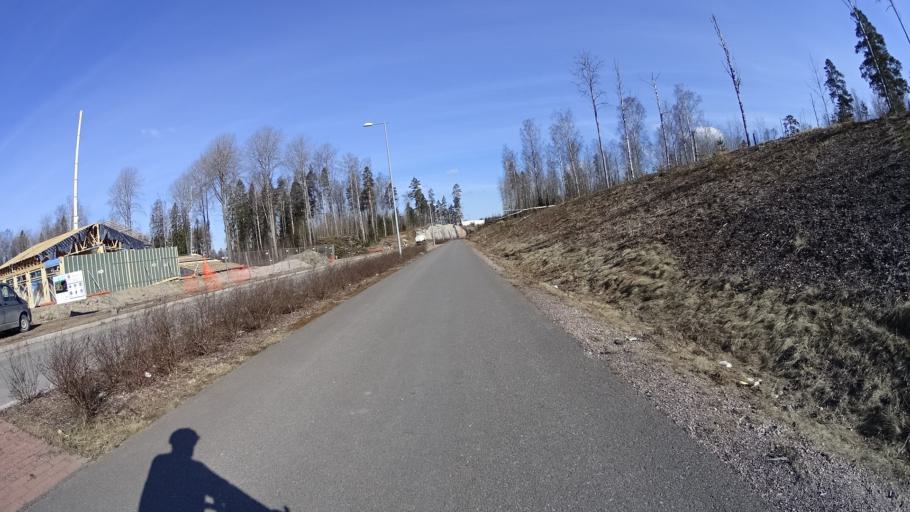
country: FI
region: Uusimaa
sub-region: Helsinki
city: Kilo
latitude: 60.2965
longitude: 24.7674
